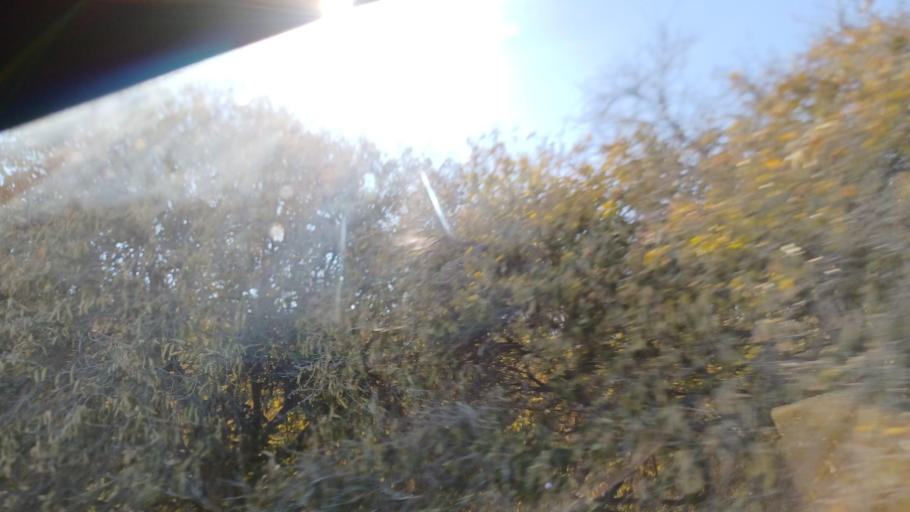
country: CY
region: Larnaka
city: Kolossi
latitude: 34.6712
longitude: 32.9497
